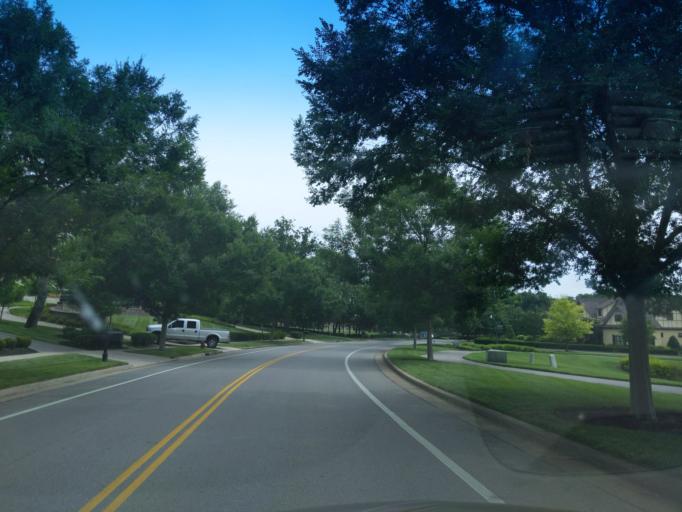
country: US
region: Tennessee
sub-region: Williamson County
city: Brentwood Estates
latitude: 36.0288
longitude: -86.7692
